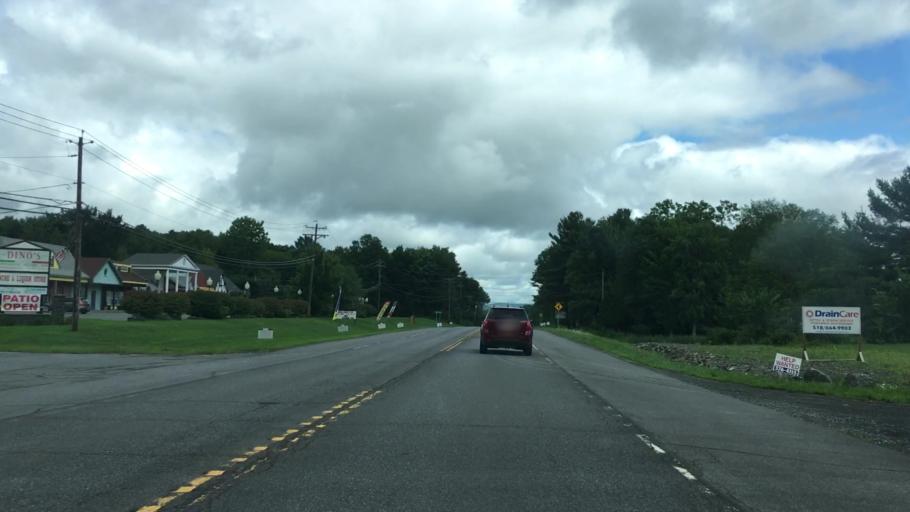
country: US
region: New York
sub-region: Rensselaer County
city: Poestenkill
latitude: 42.8068
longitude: -73.5470
